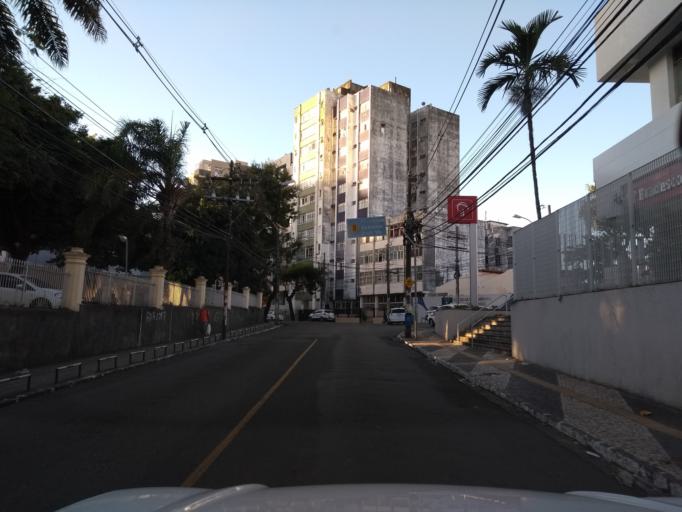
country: BR
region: Bahia
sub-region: Salvador
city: Salvador
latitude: -12.9909
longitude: -38.5185
